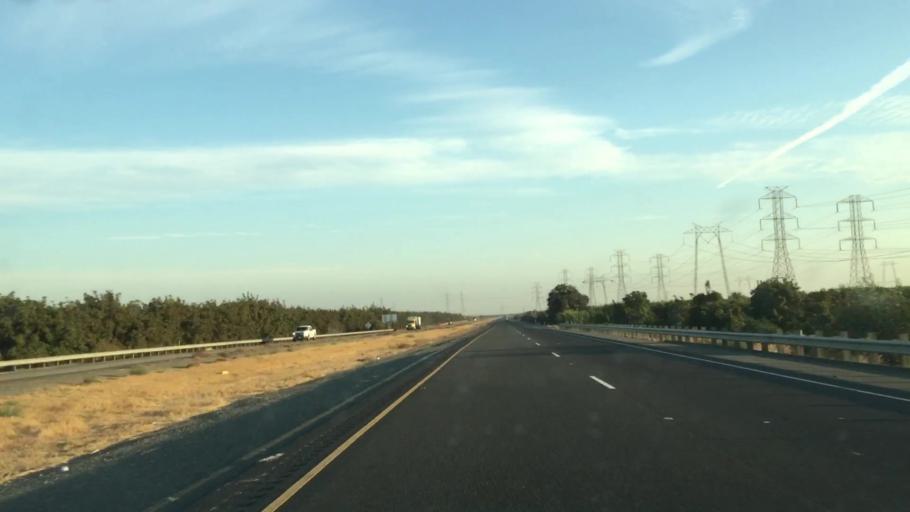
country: US
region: California
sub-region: Yolo County
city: Cottonwood
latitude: 38.6972
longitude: -121.9545
